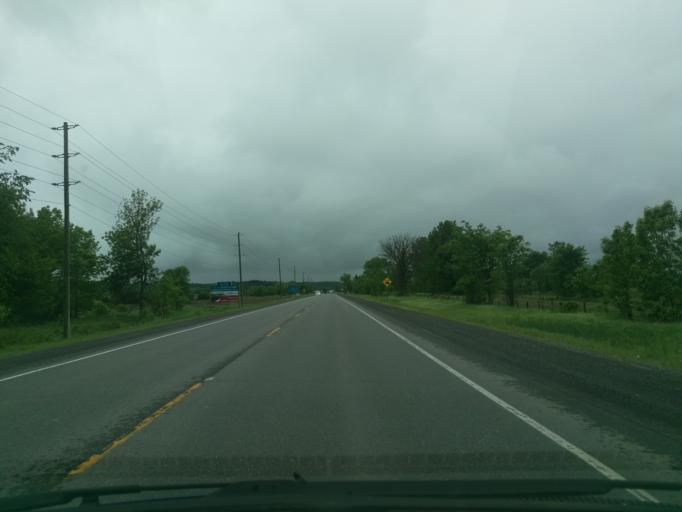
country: CA
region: Ontario
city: Clarence-Rockland
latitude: 45.5306
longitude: -75.3167
